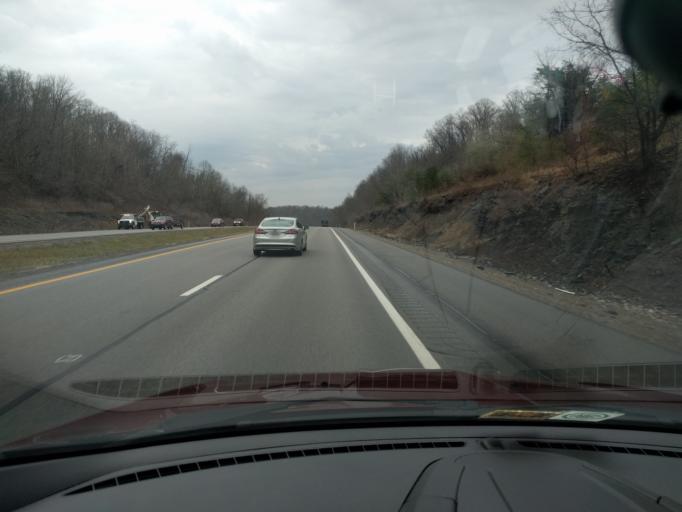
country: US
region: West Virginia
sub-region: Wood County
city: Boaz
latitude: 39.3254
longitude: -81.4659
